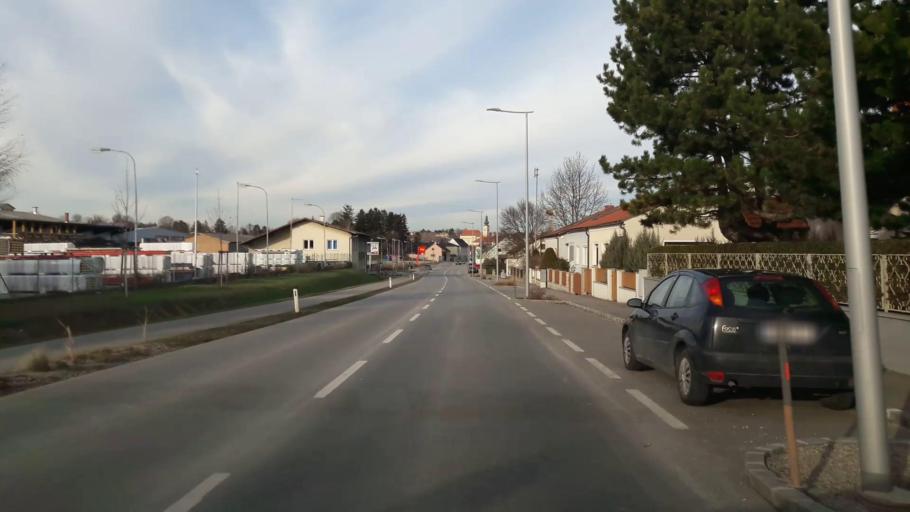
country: AT
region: Lower Austria
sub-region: Politischer Bezirk Mistelbach
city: Gaweinstal
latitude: 48.4698
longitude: 16.5894
